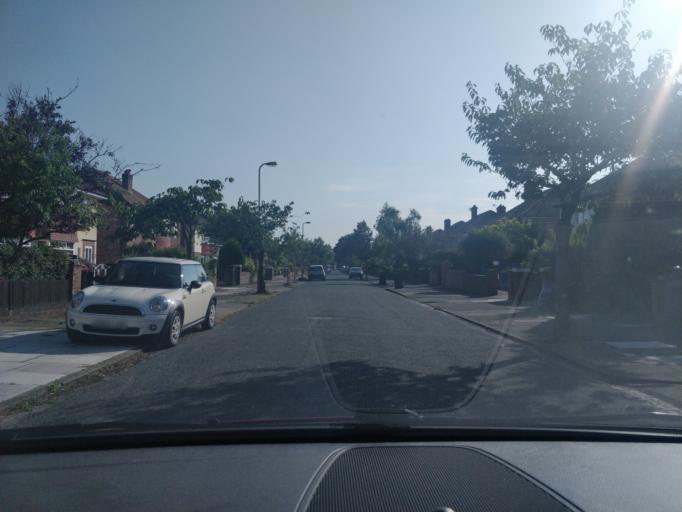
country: GB
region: England
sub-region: Sefton
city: Southport
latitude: 53.6570
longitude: -2.9714
